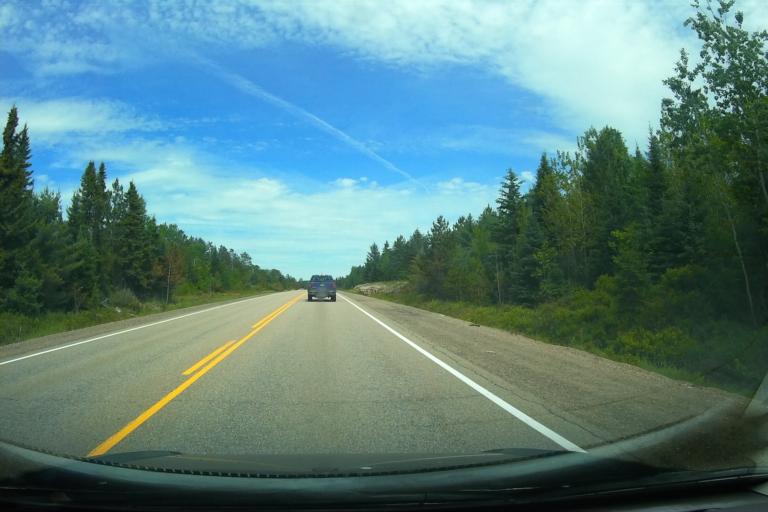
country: CA
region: Ontario
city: Mattawa
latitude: 46.2843
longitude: -78.8446
